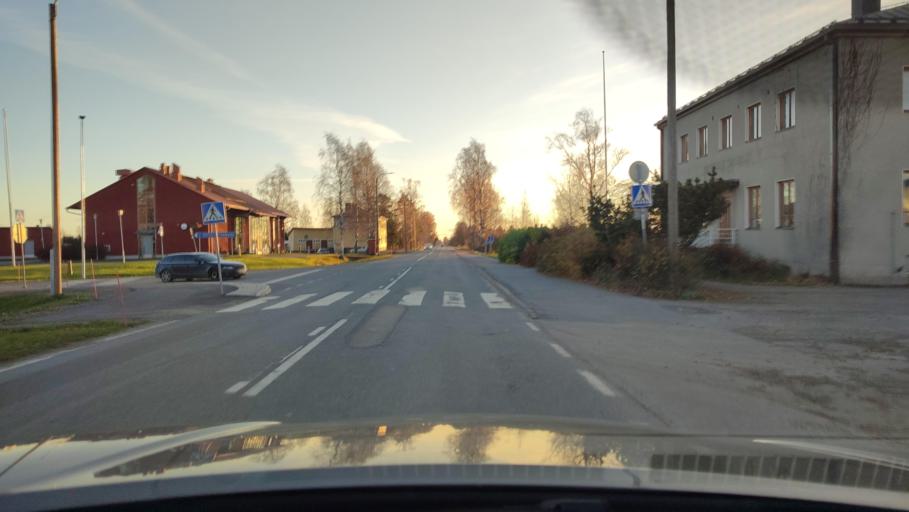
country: FI
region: Ostrobothnia
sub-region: Sydosterbotten
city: Naerpes
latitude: 62.5442
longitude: 21.3958
